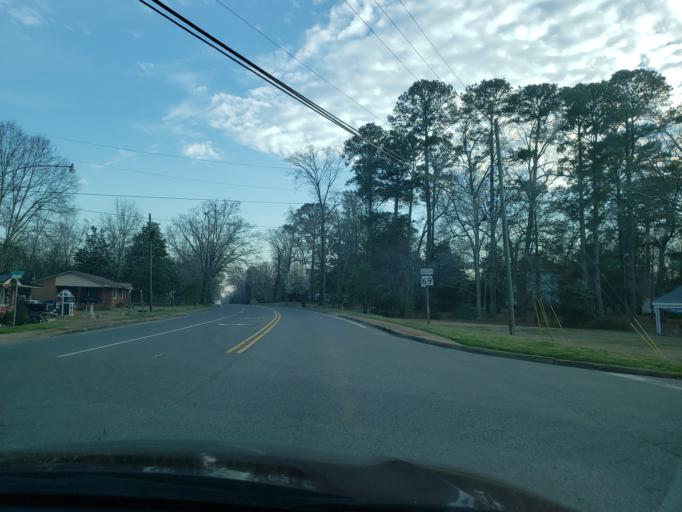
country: US
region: Alabama
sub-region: Hale County
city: Greensboro
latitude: 32.7142
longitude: -87.5959
